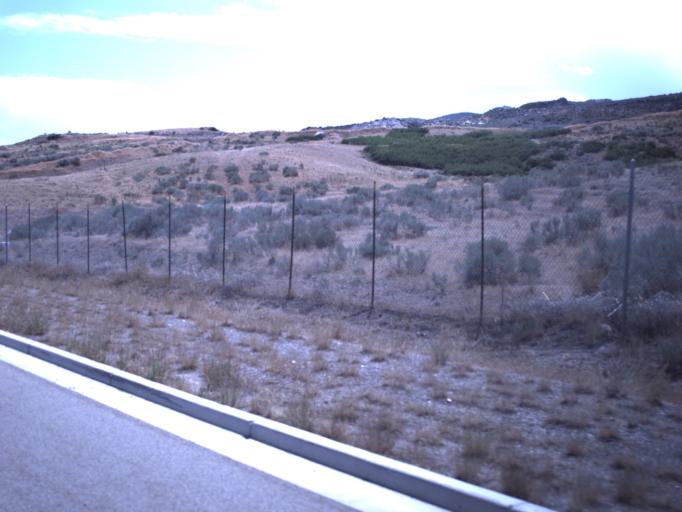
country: US
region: Utah
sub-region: Salt Lake County
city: Bluffdale
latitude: 40.4688
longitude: -111.9656
